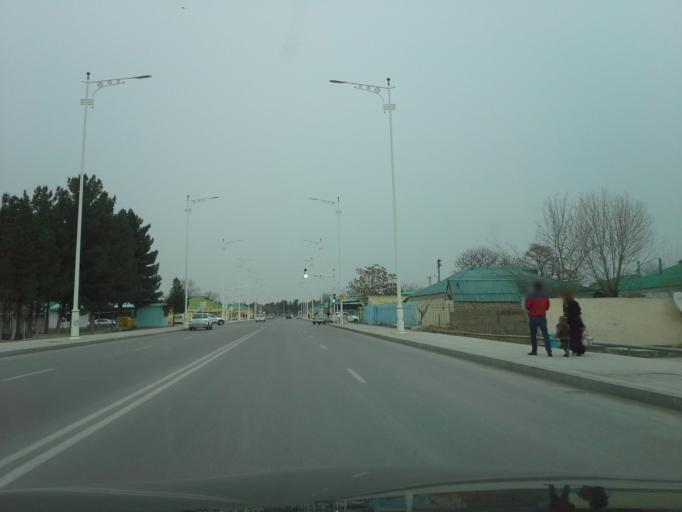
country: TM
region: Ahal
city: Ashgabat
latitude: 37.9678
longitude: 58.3486
